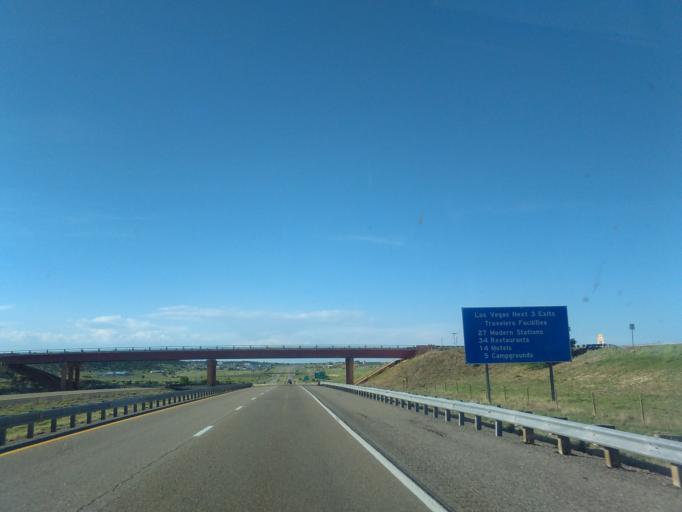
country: US
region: New Mexico
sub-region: San Miguel County
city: Las Vegas
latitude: 35.5447
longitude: -105.2276
